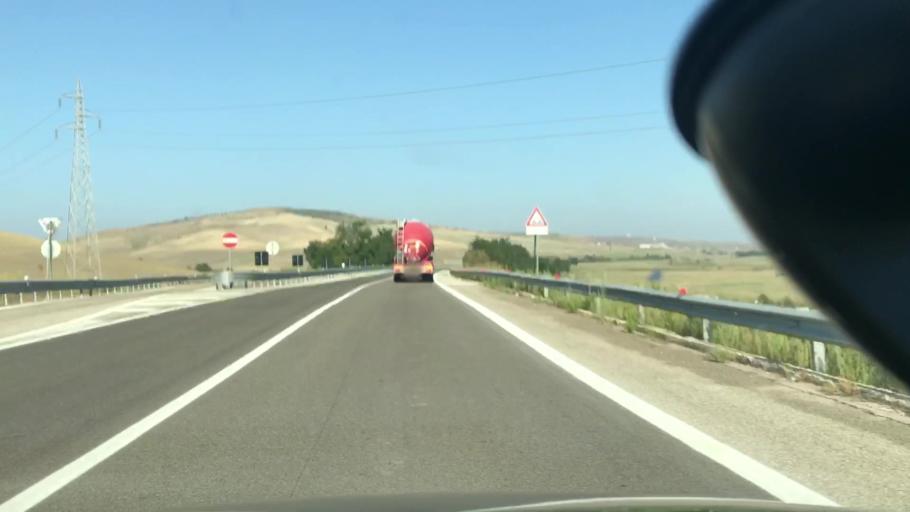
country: IT
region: Basilicate
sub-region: Provincia di Matera
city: Irsina
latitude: 40.7885
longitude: 16.2883
